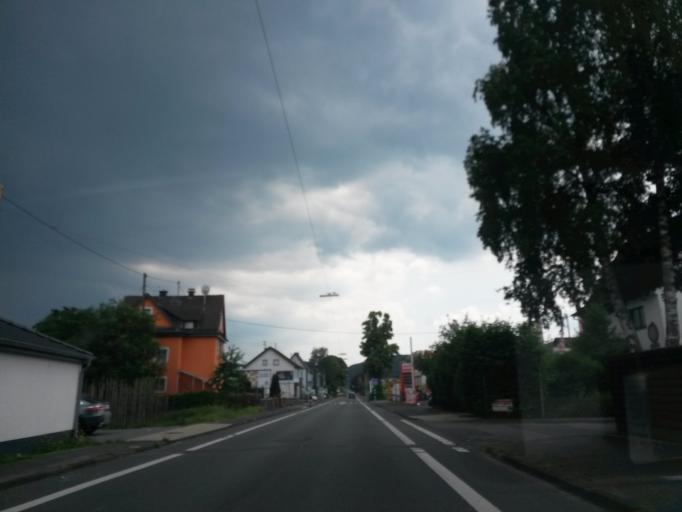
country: DE
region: North Rhine-Westphalia
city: Kreuztal
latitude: 50.9440
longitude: 7.9998
